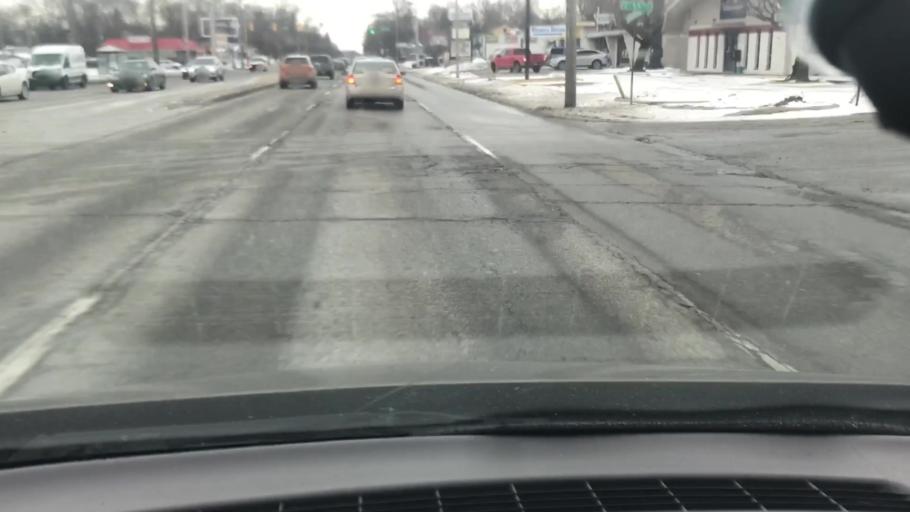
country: US
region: Indiana
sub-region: Marion County
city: Broad Ripple
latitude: 39.8538
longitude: -86.1220
